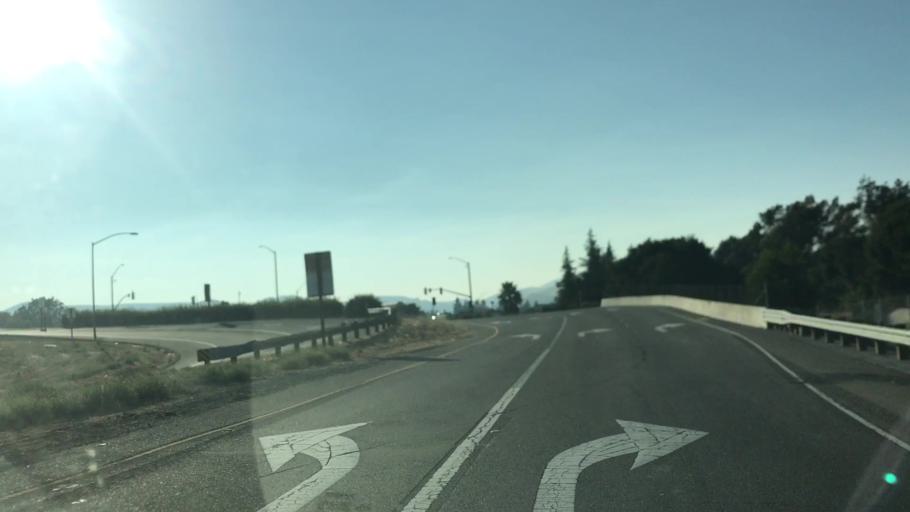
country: US
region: California
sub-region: Alameda County
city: Dublin
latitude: 37.6994
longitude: -121.9339
